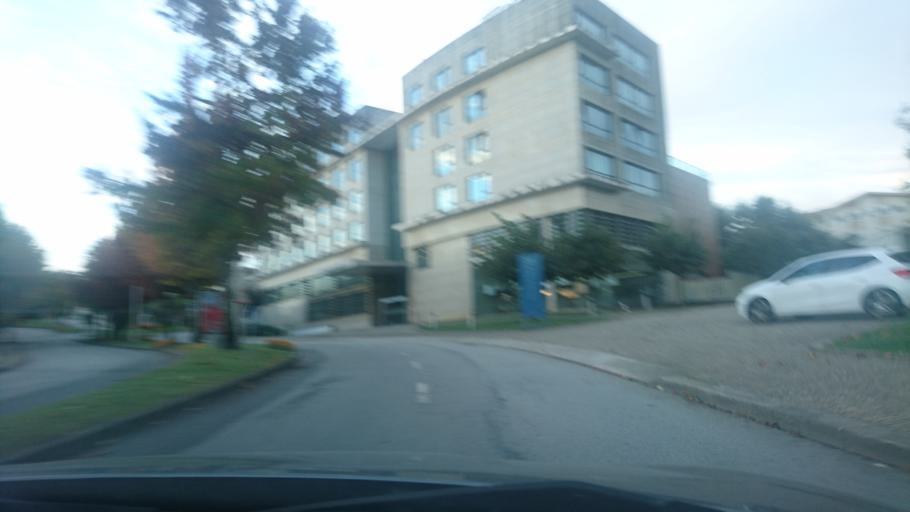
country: PT
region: Aveiro
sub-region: Sao Joao da Madeira
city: Sao Joao da Madeira
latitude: 40.8951
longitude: -8.4853
